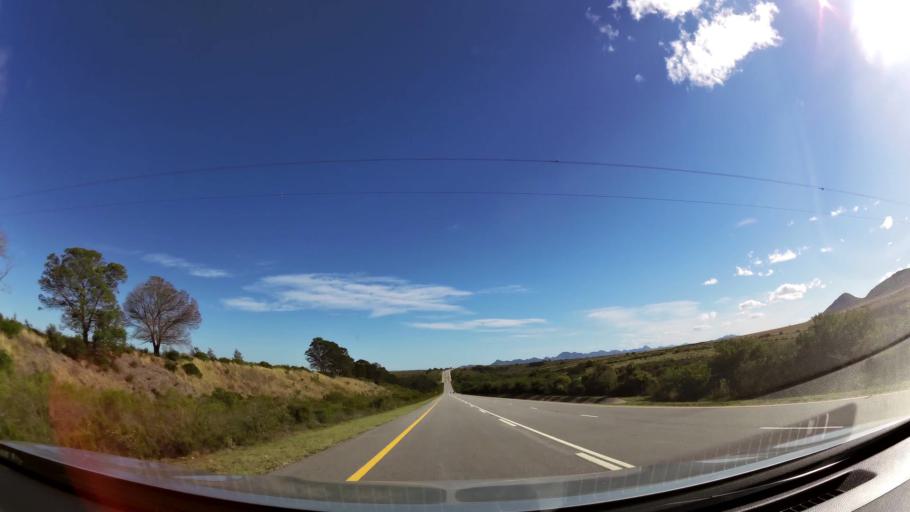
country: ZA
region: Eastern Cape
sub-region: Cacadu District Municipality
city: Kruisfontein
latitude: -34.0056
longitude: 24.6746
